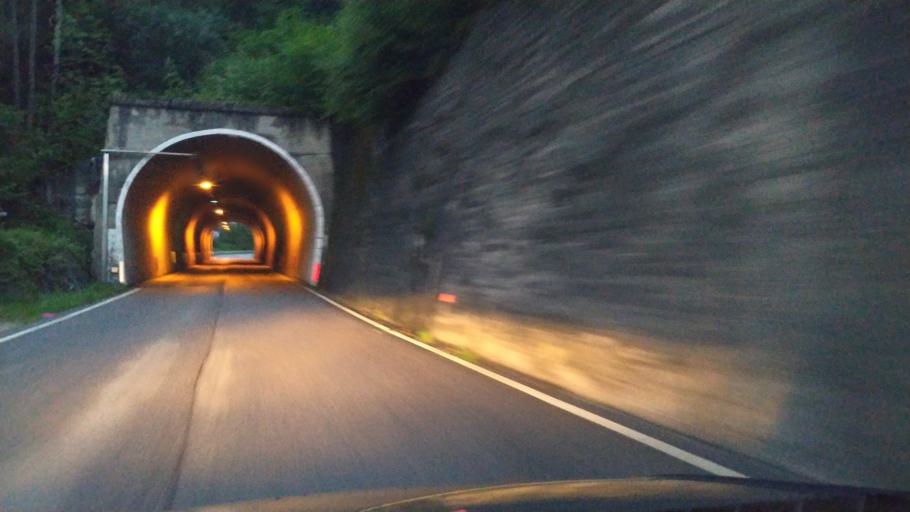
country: IT
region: Trentino-Alto Adige
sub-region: Provincia di Trento
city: Cagno
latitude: 46.3870
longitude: 11.0370
